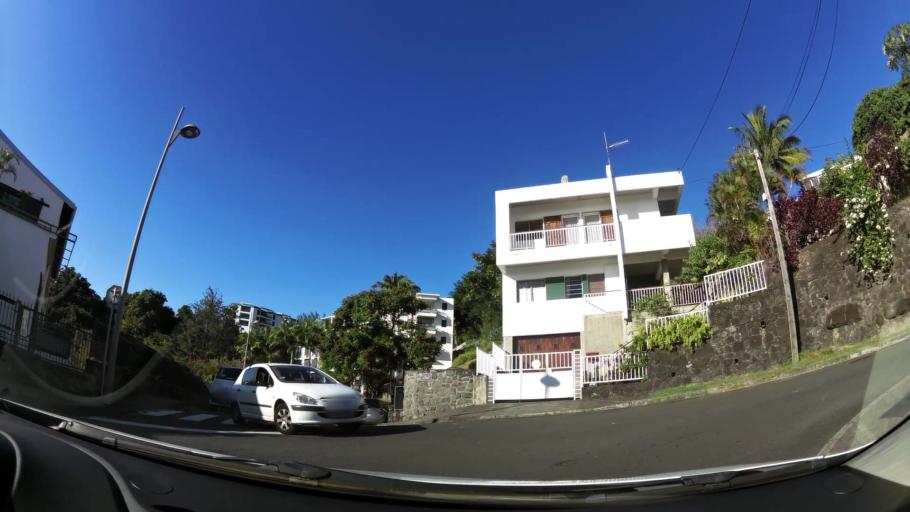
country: RE
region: Reunion
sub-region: Reunion
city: Saint-Denis
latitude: -20.8936
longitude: 55.4482
